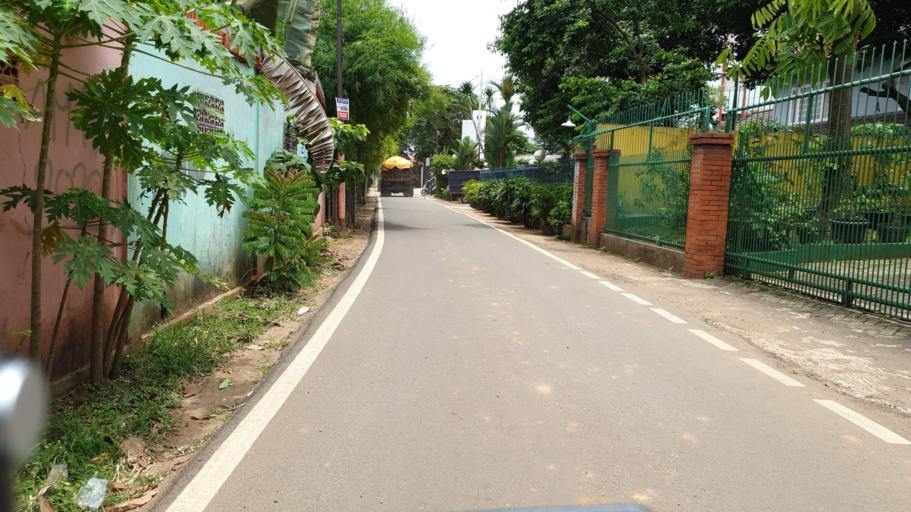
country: ID
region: West Java
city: Pamulang
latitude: -6.3085
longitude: 106.7838
